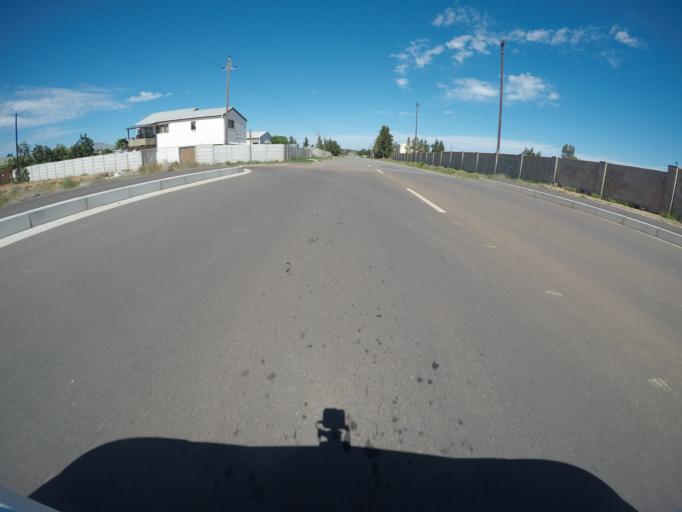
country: ZA
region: Western Cape
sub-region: West Coast District Municipality
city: Malmesbury
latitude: -33.5757
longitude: 18.6470
